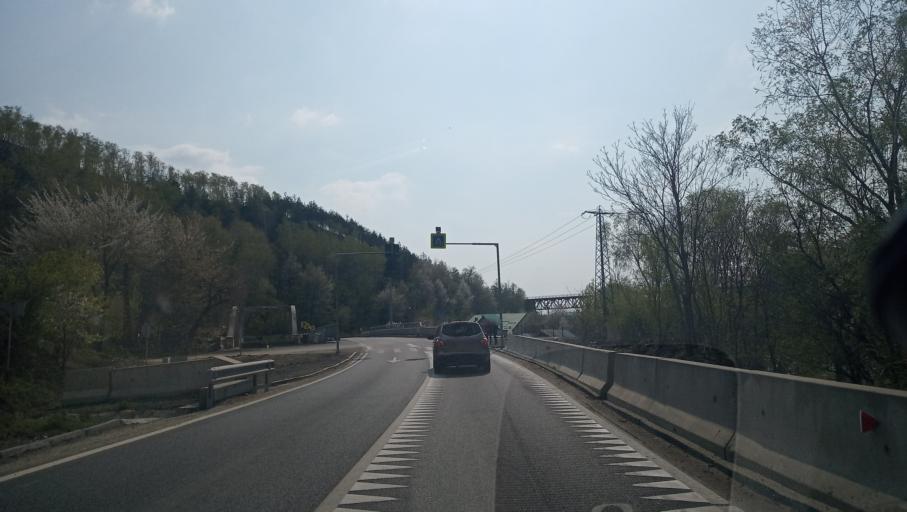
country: RO
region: Gorj
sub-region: Comuna Bumbesti-Jiu
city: Bumbesti-Jiu
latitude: 45.1896
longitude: 23.3880
